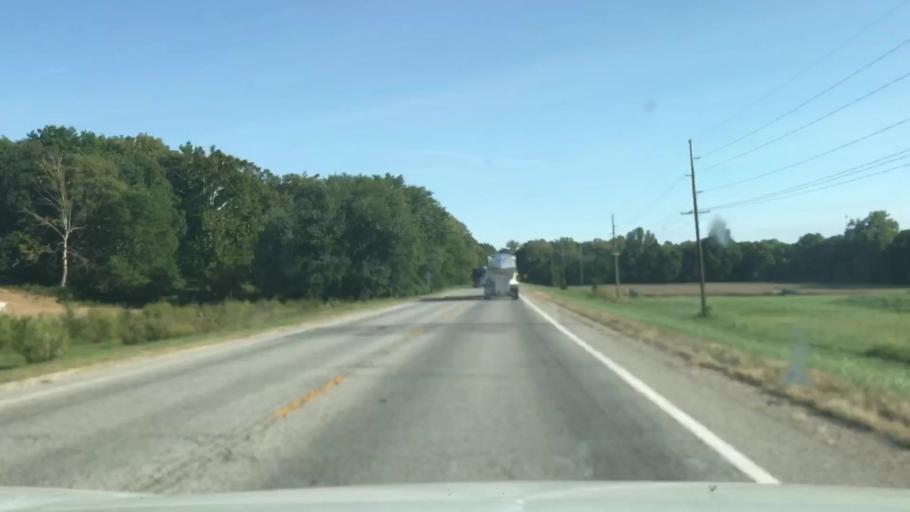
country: US
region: Illinois
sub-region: Adams County
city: Quincy
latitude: 39.8472
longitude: -91.3763
